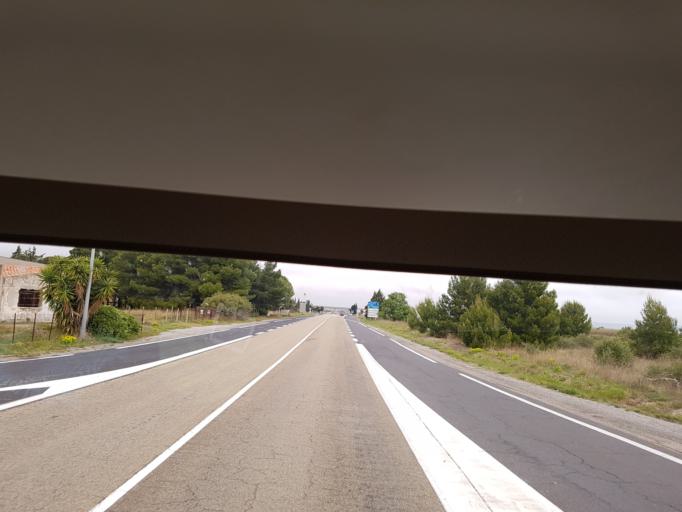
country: FR
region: Languedoc-Roussillon
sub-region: Departement de l'Aude
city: Leucate
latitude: 42.9322
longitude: 2.9925
